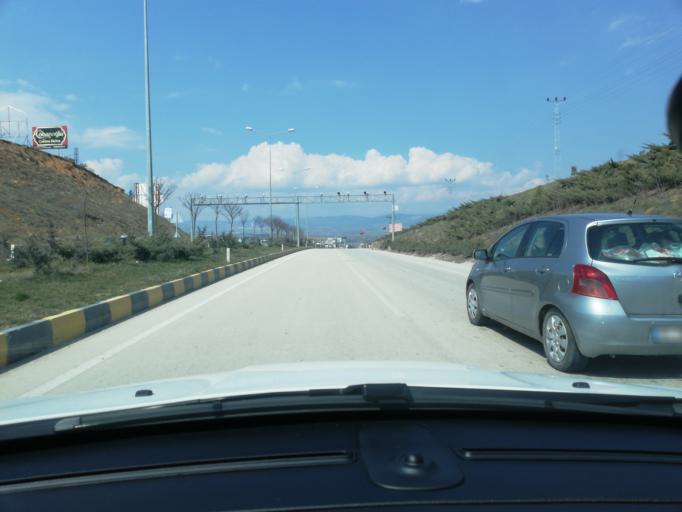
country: TR
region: Kastamonu
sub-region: Cide
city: Kastamonu
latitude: 41.4295
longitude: 33.7996
